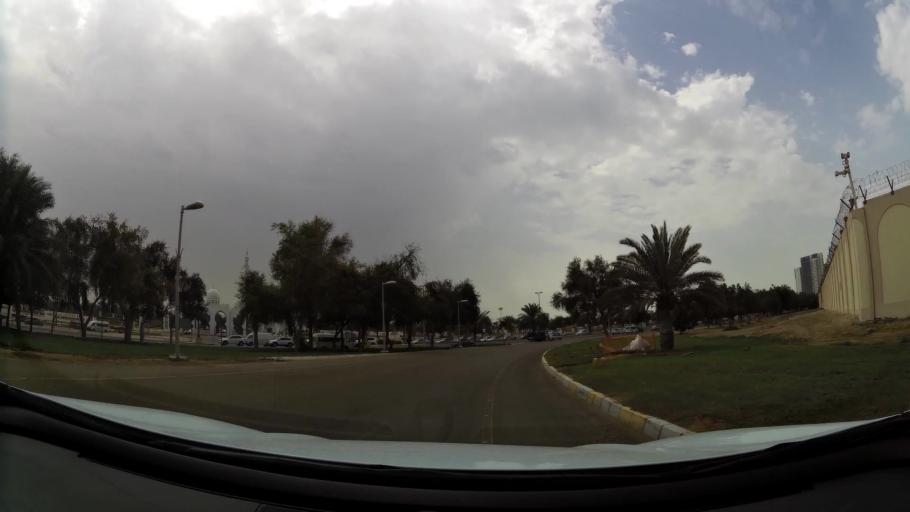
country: AE
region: Abu Dhabi
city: Abu Dhabi
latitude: 24.4182
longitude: 54.4737
